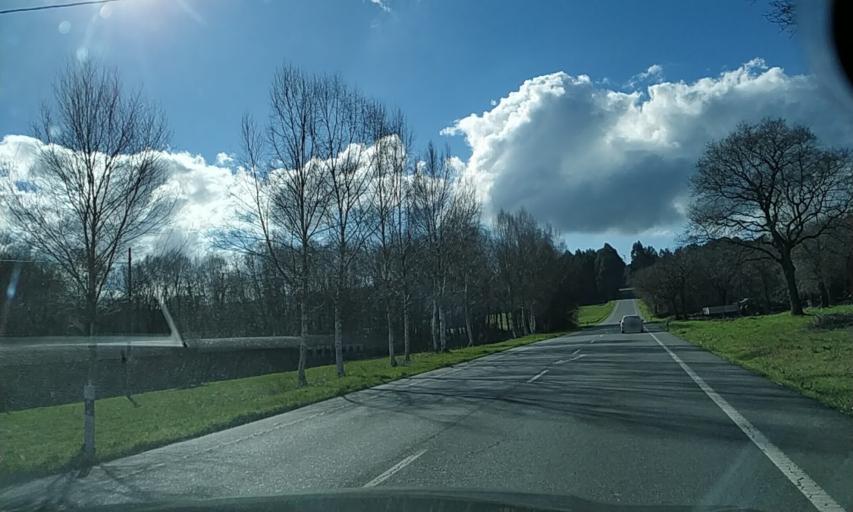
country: ES
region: Galicia
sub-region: Provincia de Pontevedra
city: Silleda
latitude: 42.7070
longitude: -8.3007
